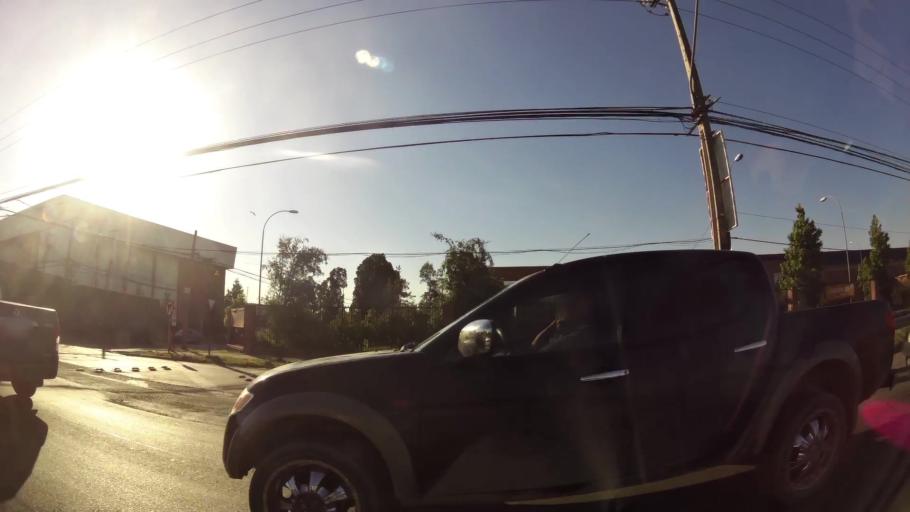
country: CL
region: Santiago Metropolitan
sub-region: Provincia de Maipo
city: San Bernardo
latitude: -33.5415
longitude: -70.7412
